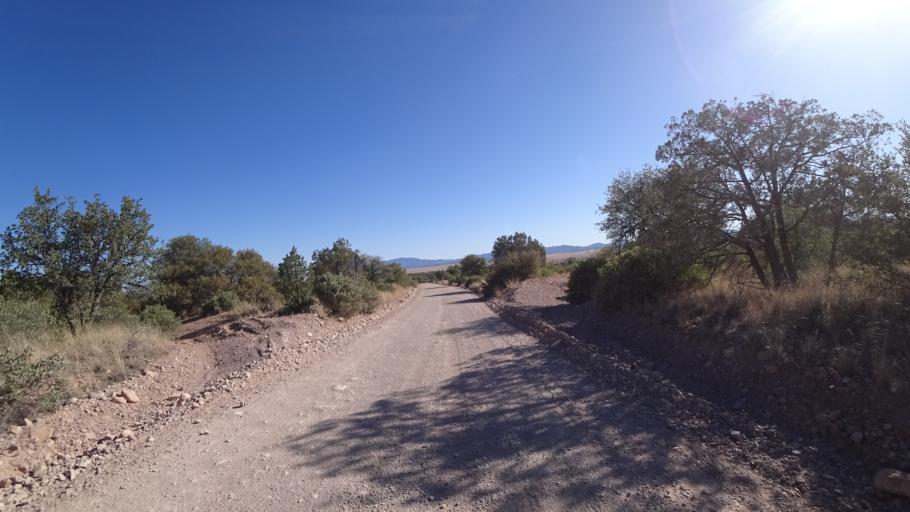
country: US
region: Arizona
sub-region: Cochise County
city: Huachuca City
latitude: 31.4950
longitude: -110.5542
